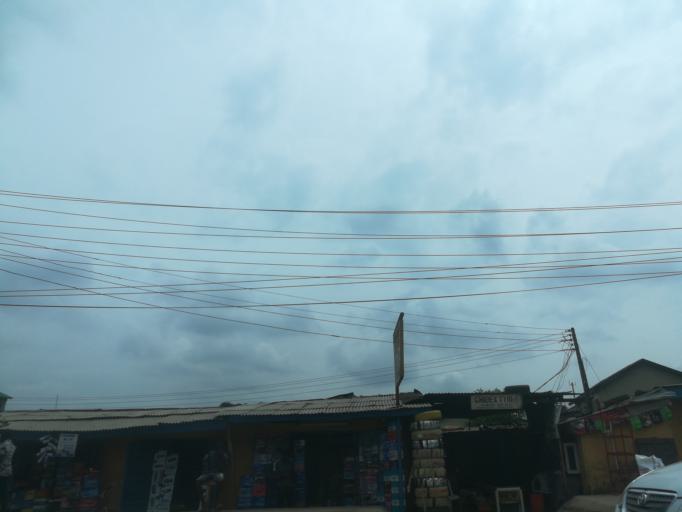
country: NG
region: Lagos
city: Ikeja
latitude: 6.5920
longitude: 3.3394
